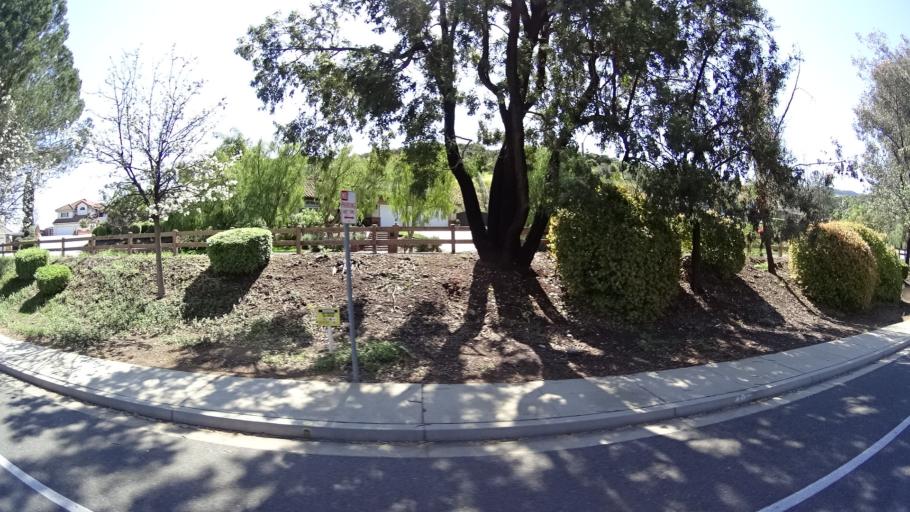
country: US
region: California
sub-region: Ventura County
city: Casa Conejo
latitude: 34.1677
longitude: -118.9369
